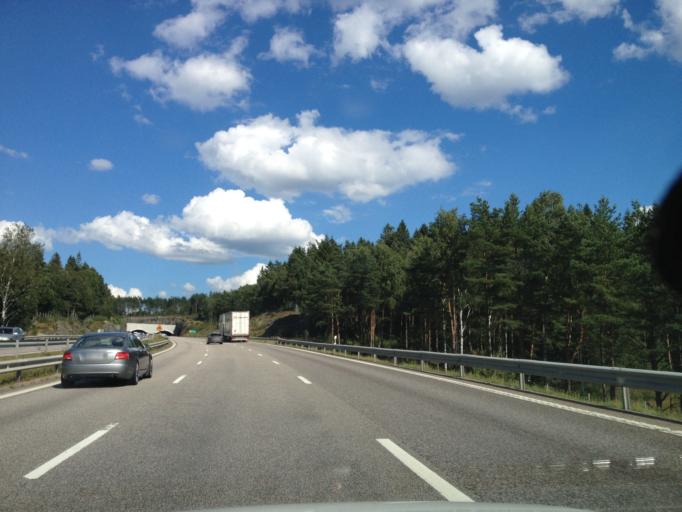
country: SE
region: Vaestra Goetaland
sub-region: Partille Kommun
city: Furulund
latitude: 57.7403
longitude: 12.1760
